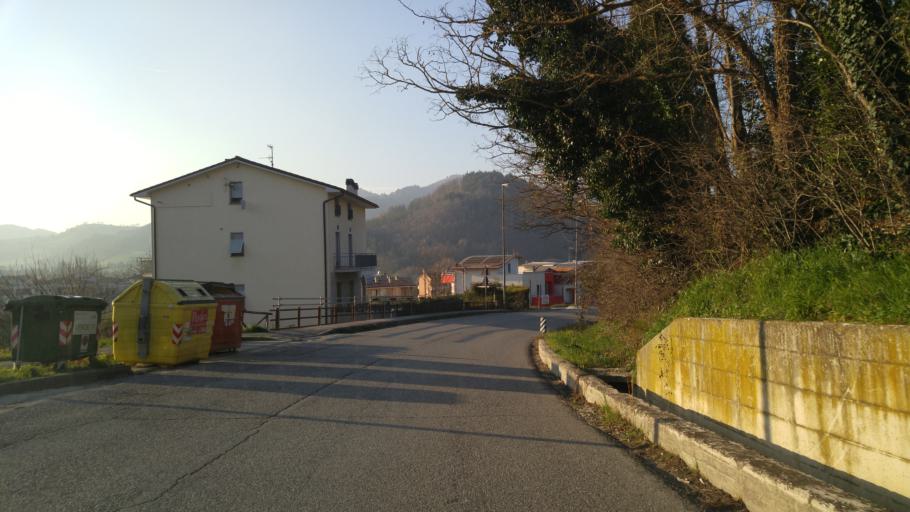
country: IT
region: The Marches
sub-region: Provincia di Pesaro e Urbino
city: Fermignano
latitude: 43.6717
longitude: 12.6489
